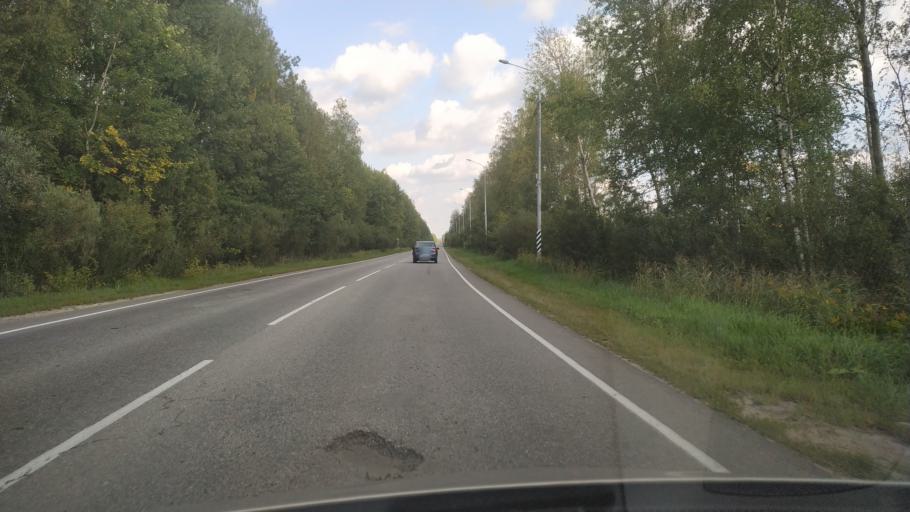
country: RU
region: Moskovskaya
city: Likino-Dulevo
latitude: 55.7292
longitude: 39.0155
